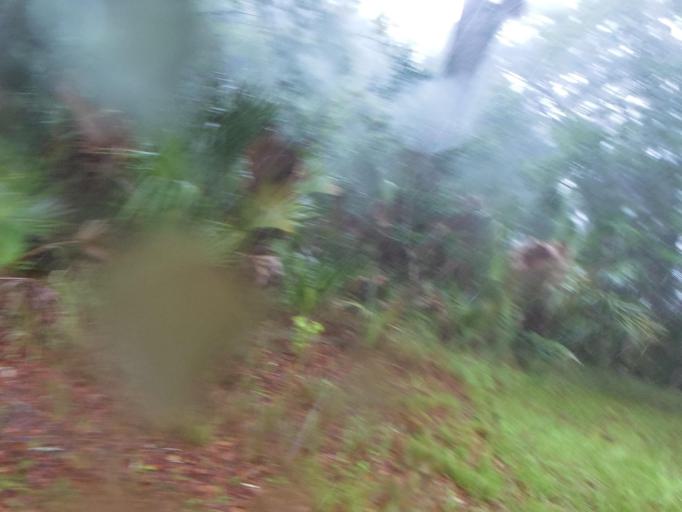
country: US
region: Florida
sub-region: Putnam County
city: Palatka
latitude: 29.6785
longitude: -81.7491
